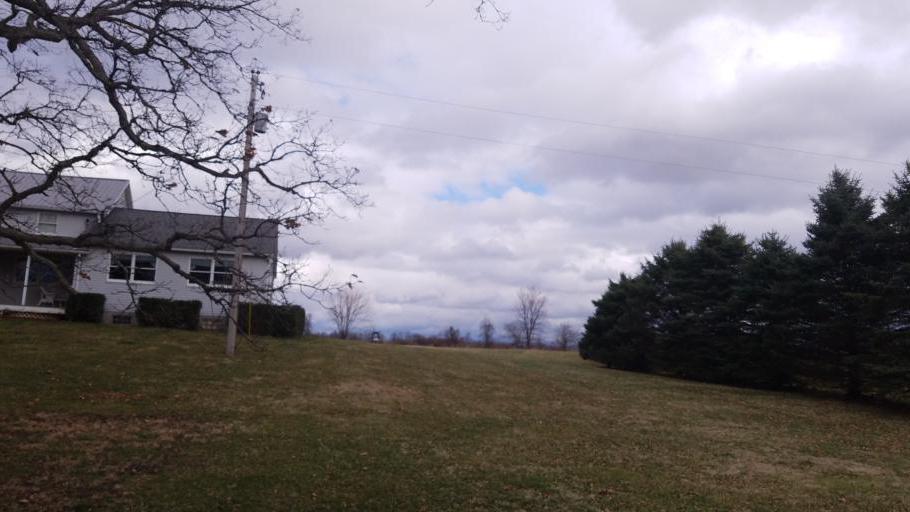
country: US
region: Ohio
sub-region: Knox County
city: Mount Vernon
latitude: 40.3269
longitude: -82.5323
